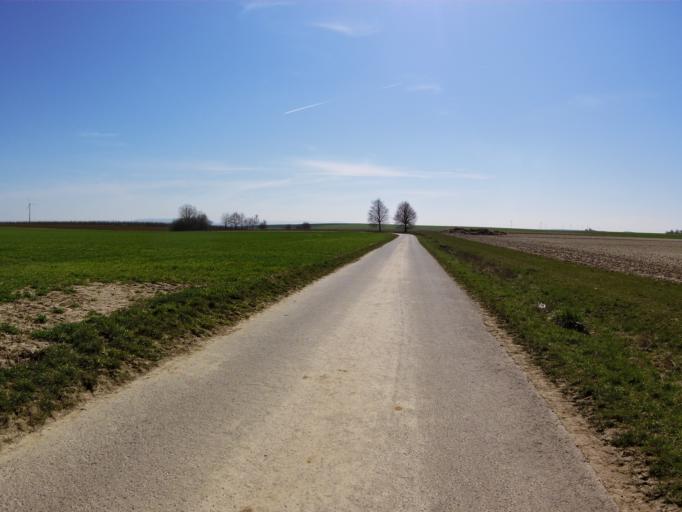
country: DE
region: Bavaria
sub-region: Regierungsbezirk Unterfranken
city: Prosselsheim
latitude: 49.8466
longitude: 10.1242
